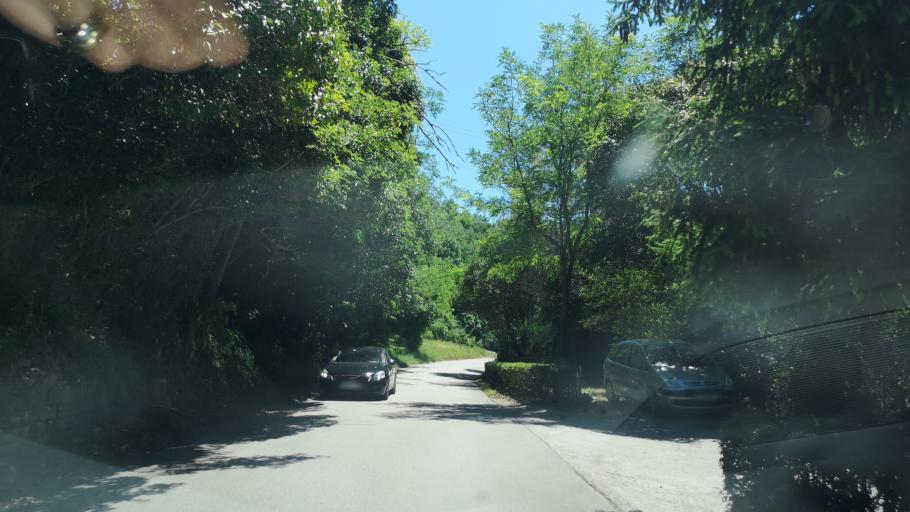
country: SI
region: Piran-Pirano
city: Portoroz
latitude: 45.5208
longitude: 13.5852
